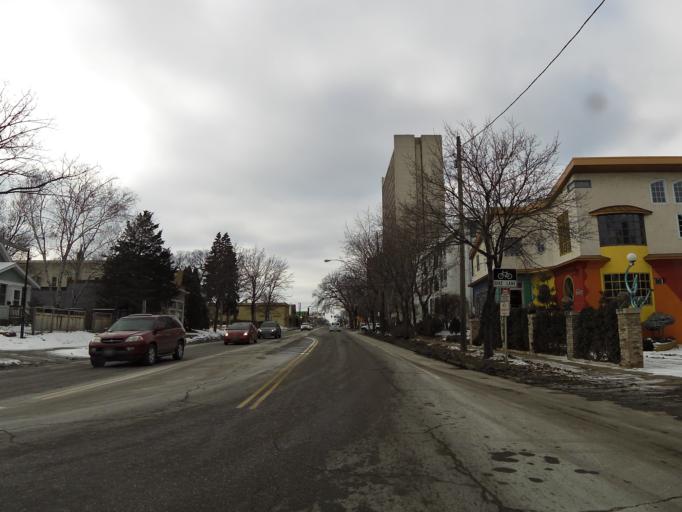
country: US
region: Minnesota
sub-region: Hennepin County
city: Minneapolis
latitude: 44.9628
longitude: -93.2269
